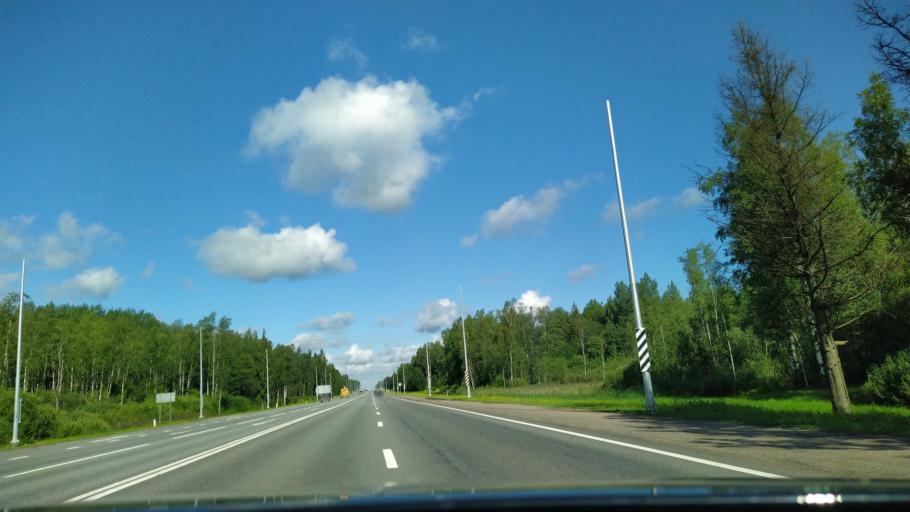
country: RU
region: Leningrad
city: Ul'yanovka
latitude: 59.5846
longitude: 30.7978
